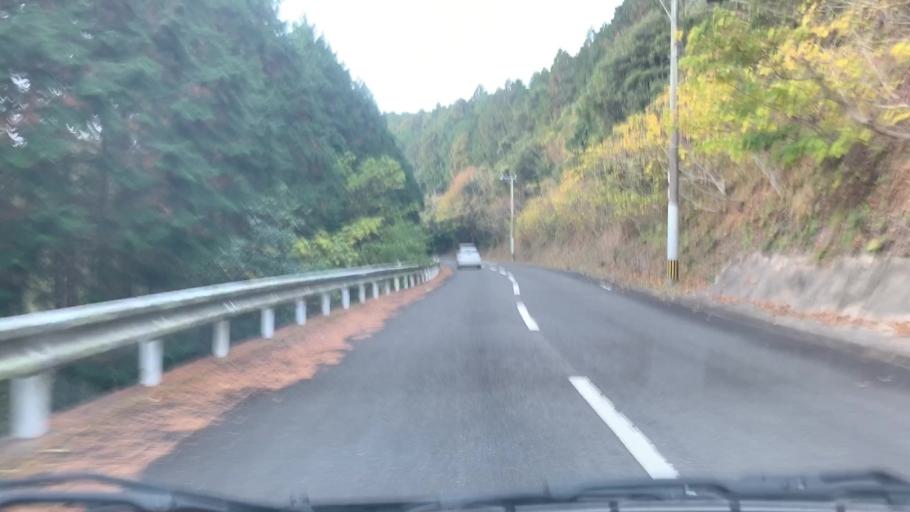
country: JP
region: Nagasaki
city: Togitsu
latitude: 32.9008
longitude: 129.7275
